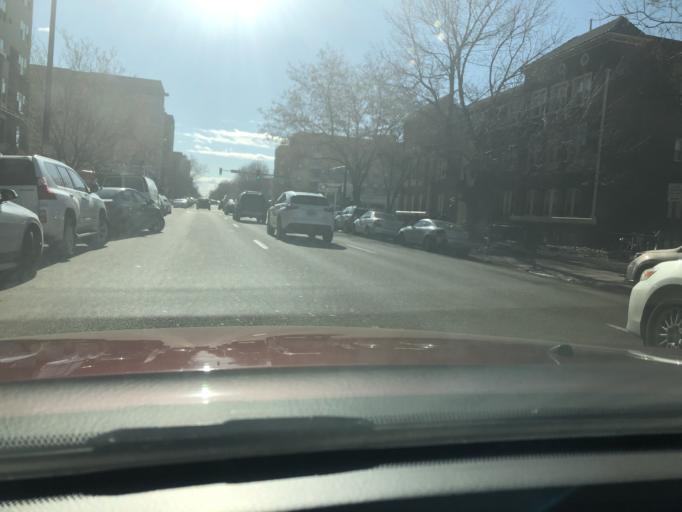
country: US
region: Colorado
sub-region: Denver County
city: Denver
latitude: 39.7375
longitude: -104.9836
